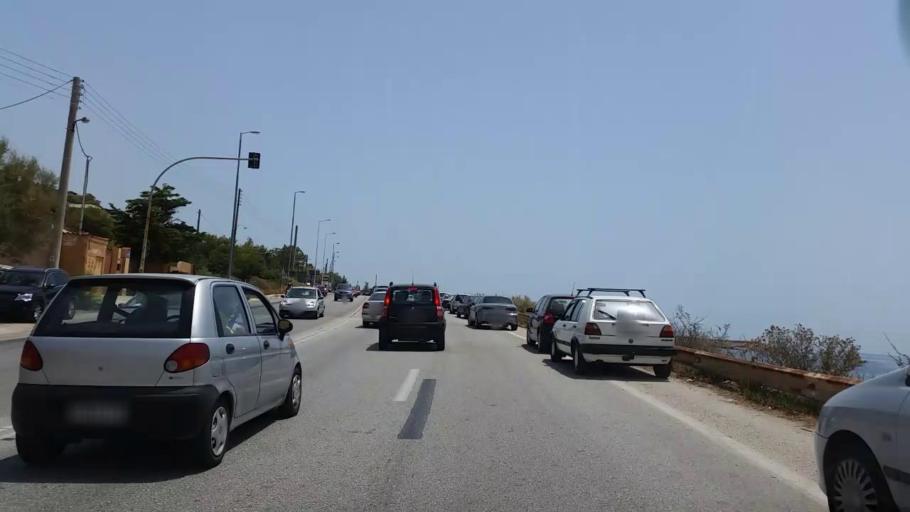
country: GR
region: Attica
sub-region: Nomarchia Anatolikis Attikis
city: Agia Marina
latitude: 37.8130
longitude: 23.8440
